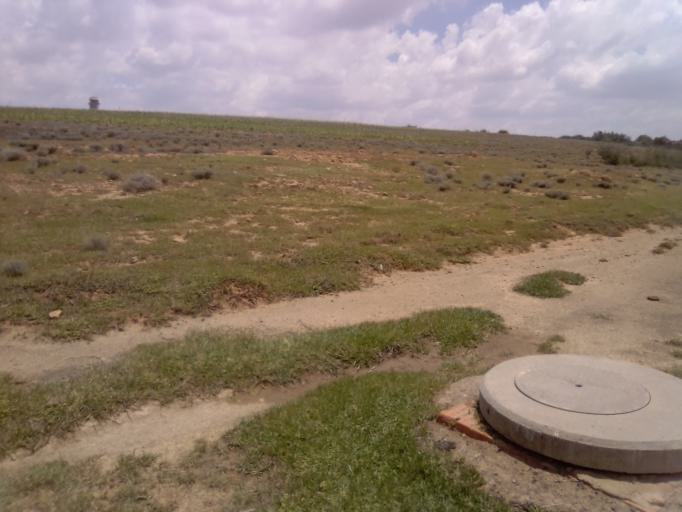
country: LS
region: Maseru
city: Maseru
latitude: -29.4599
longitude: 27.5618
